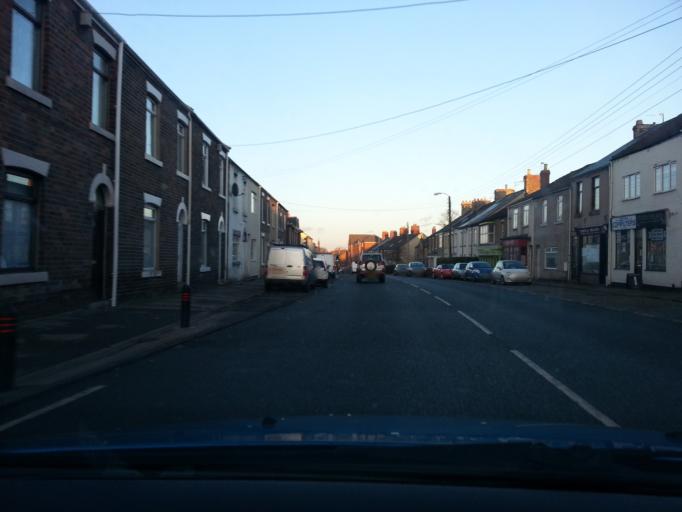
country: GB
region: England
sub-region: County Durham
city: Ushaw Moor
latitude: 54.7505
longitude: -1.6202
